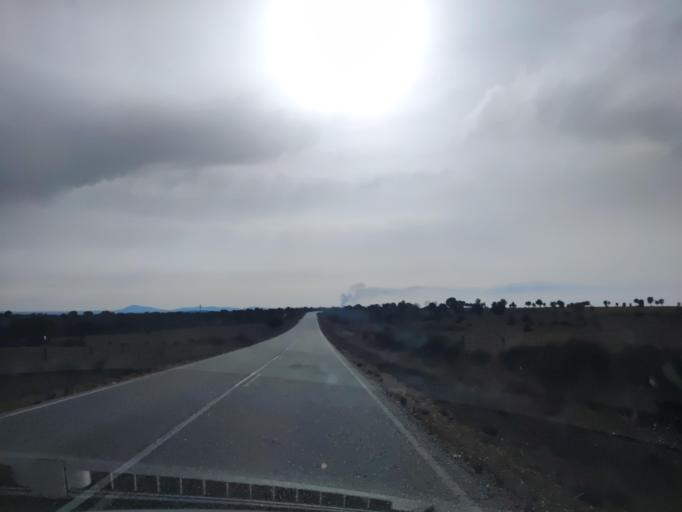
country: ES
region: Castille and Leon
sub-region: Provincia de Salamanca
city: Fuentes de Onoro
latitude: 40.6360
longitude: -6.8044
